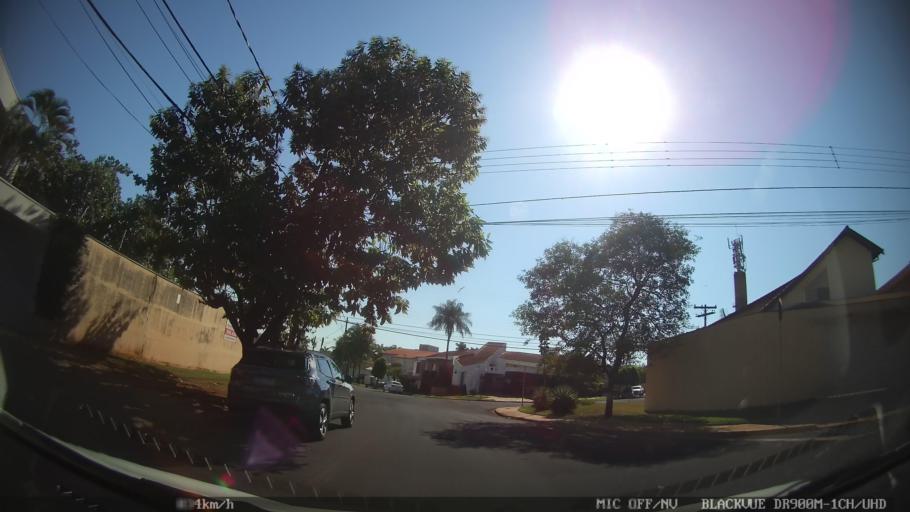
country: BR
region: Sao Paulo
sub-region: Ribeirao Preto
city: Ribeirao Preto
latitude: -21.1994
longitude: -47.8142
